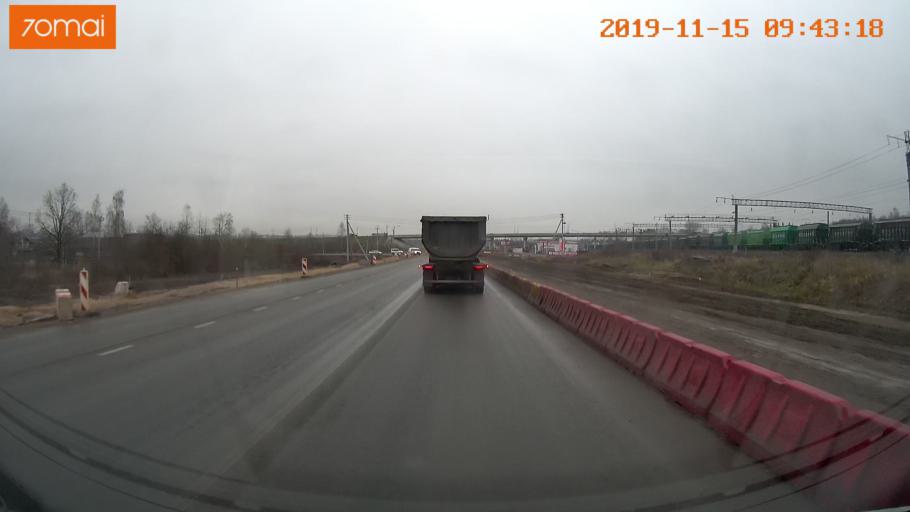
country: RU
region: Vologda
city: Sheksna
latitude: 59.2101
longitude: 38.5094
